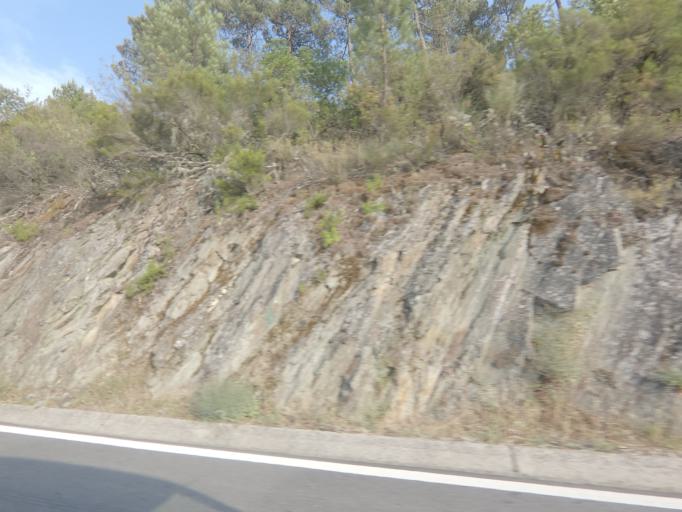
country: PT
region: Viseu
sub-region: Tabuaco
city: Tabuaco
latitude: 41.1487
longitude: -7.6189
